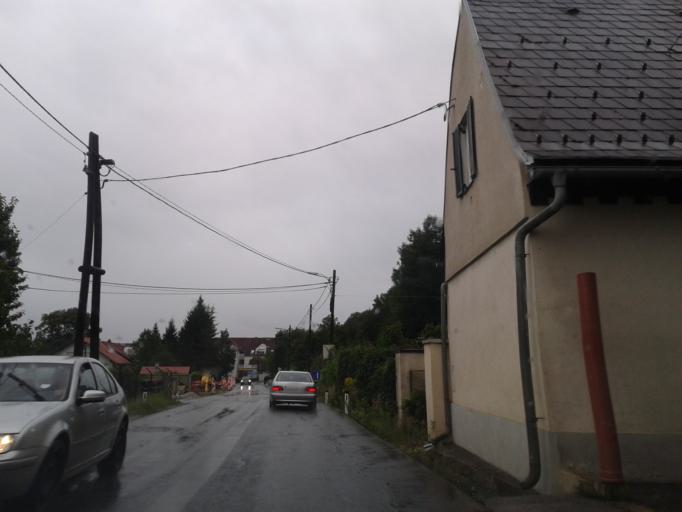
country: AT
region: Styria
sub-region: Graz Stadt
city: Goesting
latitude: 47.0848
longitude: 15.4032
